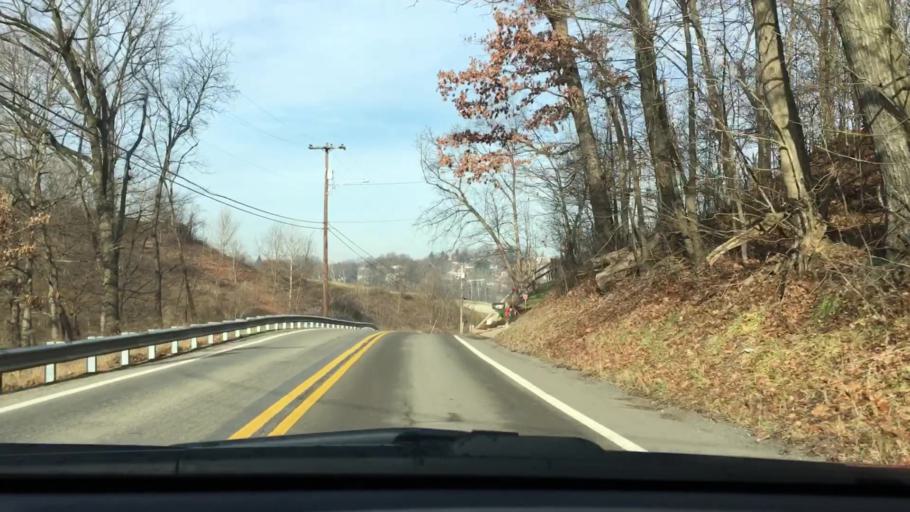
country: US
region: Pennsylvania
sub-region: Allegheny County
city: Jefferson Hills
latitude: 40.2759
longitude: -79.9488
